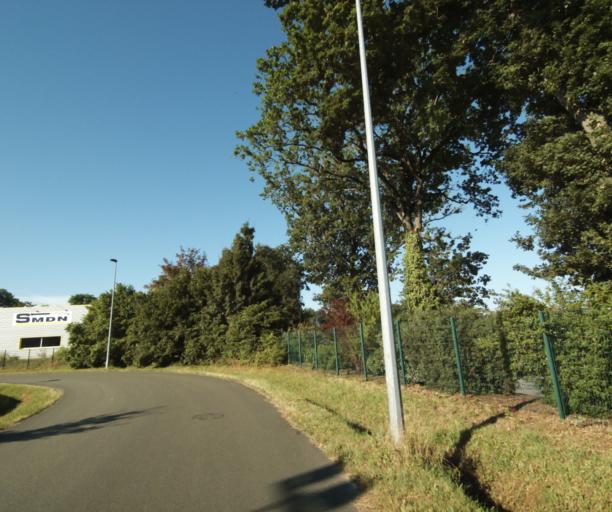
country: FR
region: Pays de la Loire
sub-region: Departement de la Mayenne
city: Laval
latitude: 48.0527
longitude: -0.7370
